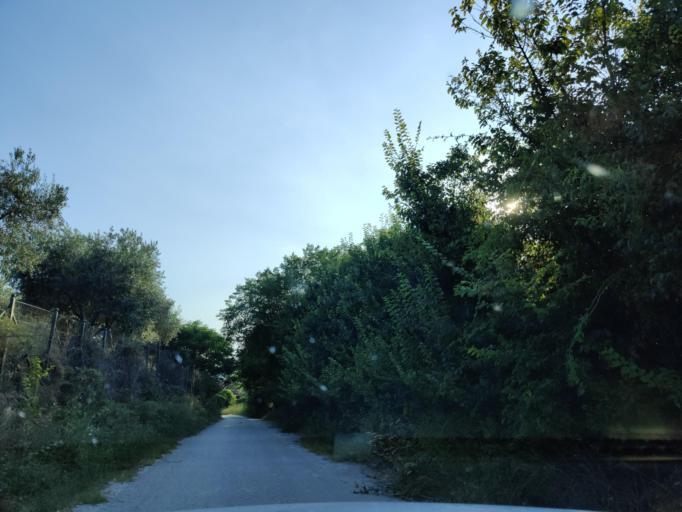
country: GR
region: East Macedonia and Thrace
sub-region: Nomos Kavalas
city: Nea Peramos
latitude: 40.8300
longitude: 24.2971
